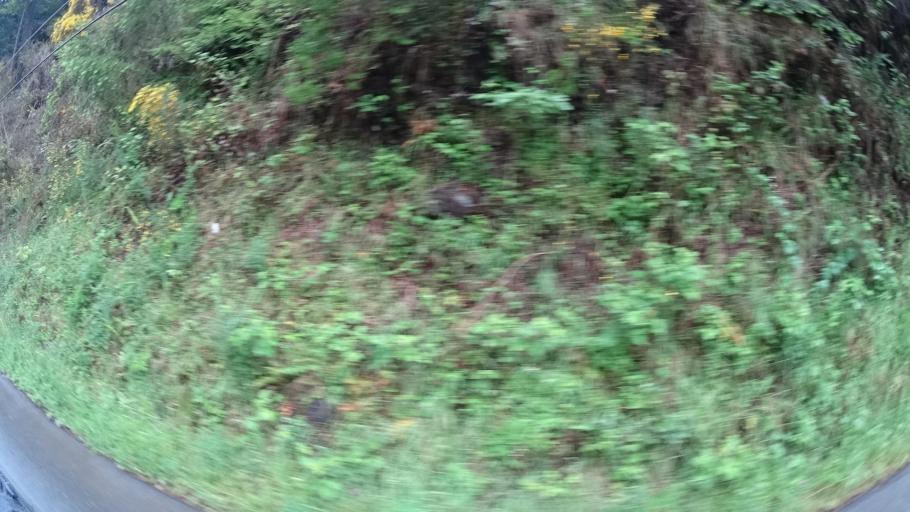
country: US
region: California
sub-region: Humboldt County
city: Bayside
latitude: 40.8154
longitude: -124.0269
